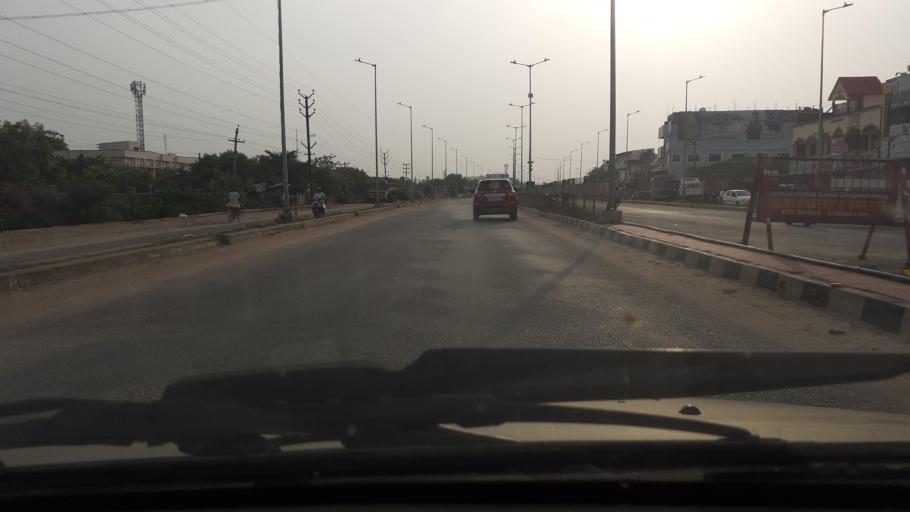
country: IN
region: Tamil Nadu
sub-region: Tirunelveli Kattabo
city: Tirunelveli
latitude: 8.7137
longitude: 77.7730
